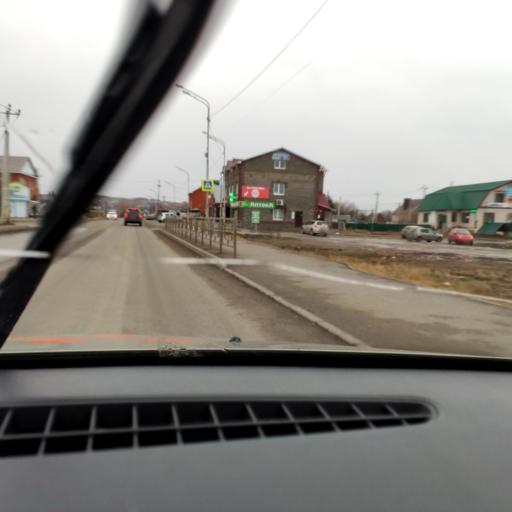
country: RU
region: Bashkortostan
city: Ufa
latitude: 54.6138
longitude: 55.9362
